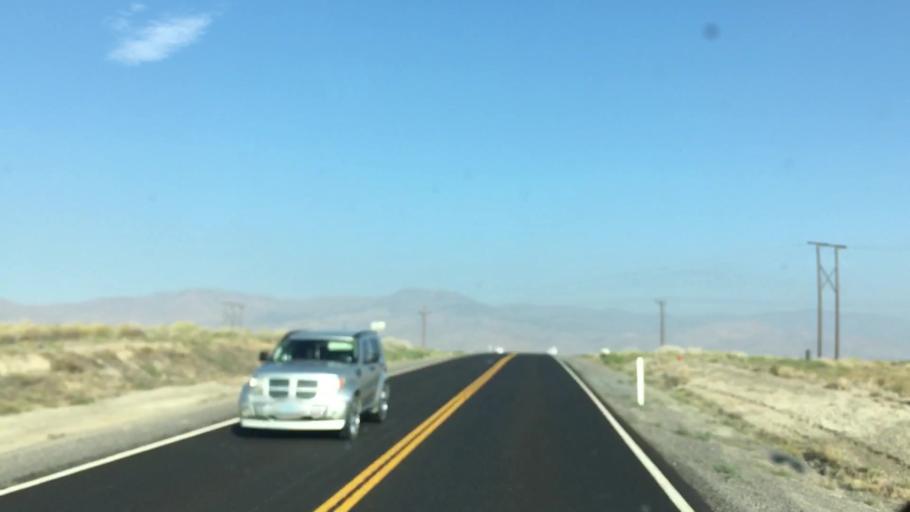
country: US
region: Nevada
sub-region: Lyon County
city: Fernley
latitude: 39.6405
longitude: -119.2976
